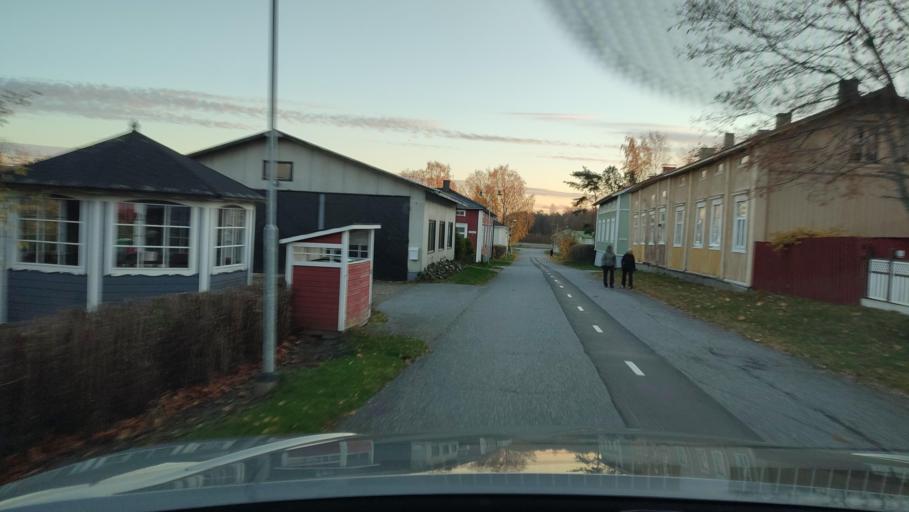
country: FI
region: Ostrobothnia
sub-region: Sydosterbotten
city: Kristinestad
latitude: 62.2688
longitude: 21.3745
